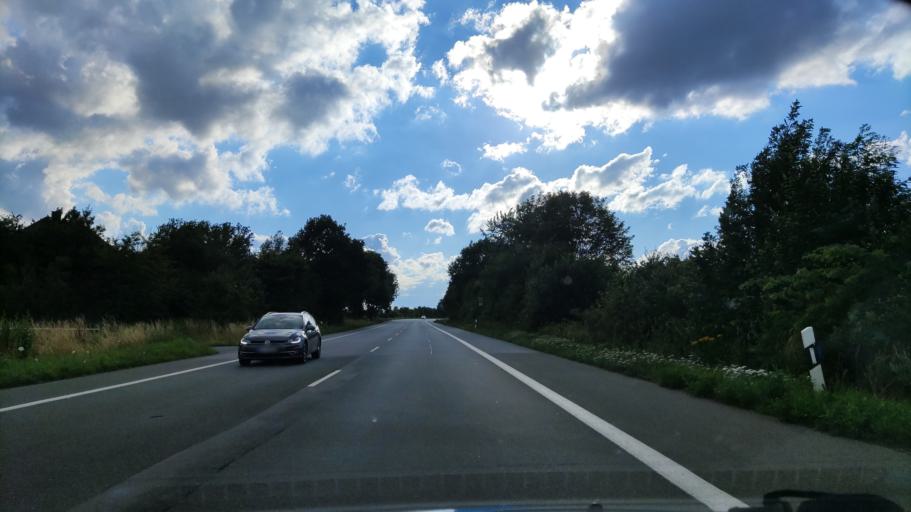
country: DE
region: North Rhine-Westphalia
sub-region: Regierungsbezirk Munster
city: Drensteinfurt
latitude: 51.7898
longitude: 7.7798
